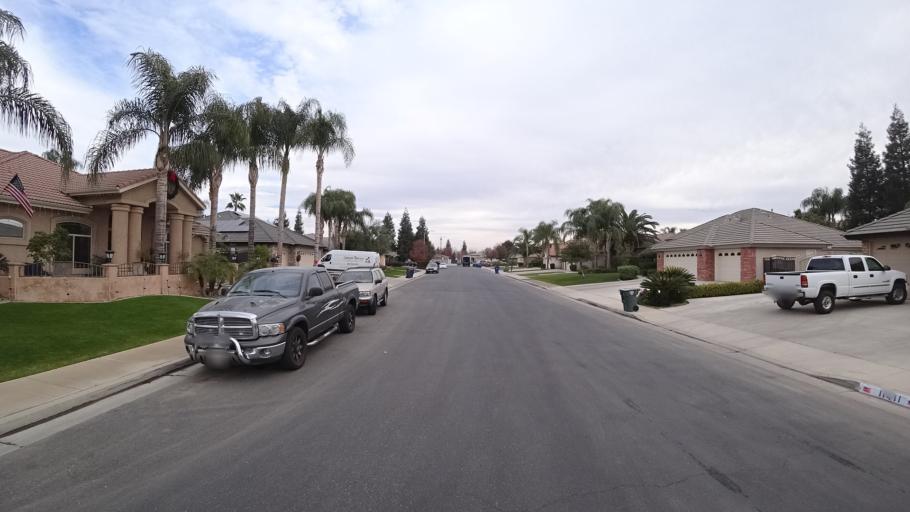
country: US
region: California
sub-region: Kern County
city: Rosedale
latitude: 35.4148
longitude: -119.1301
